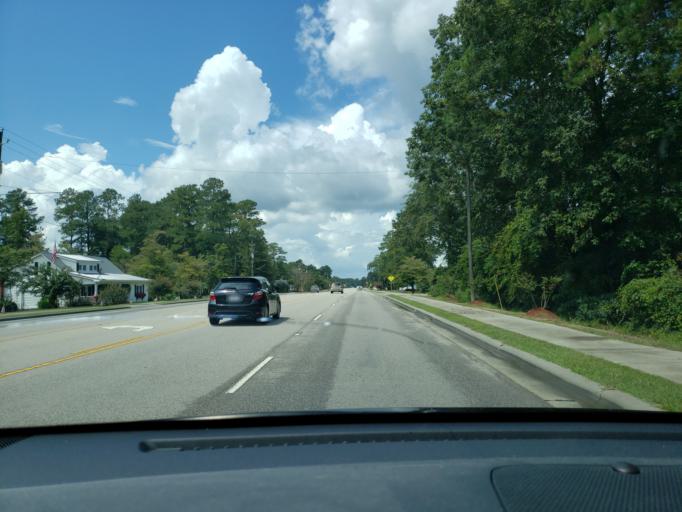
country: US
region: North Carolina
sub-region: Bladen County
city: Elizabethtown
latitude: 34.6519
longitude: -78.7152
